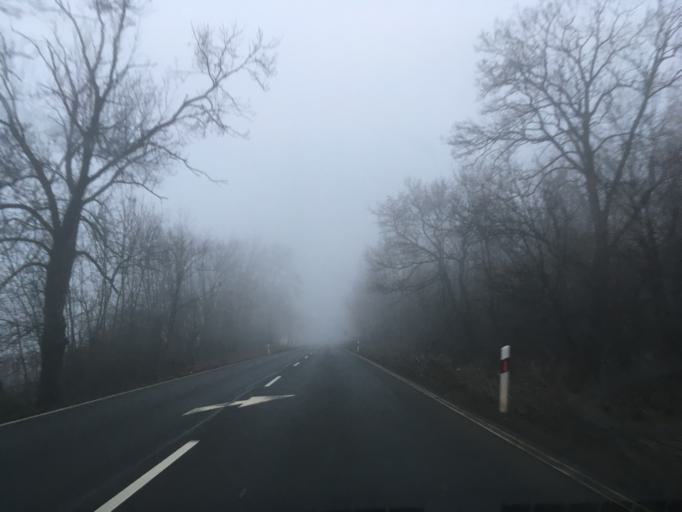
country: HU
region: Heves
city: Kerecsend
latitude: 47.8200
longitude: 20.3579
